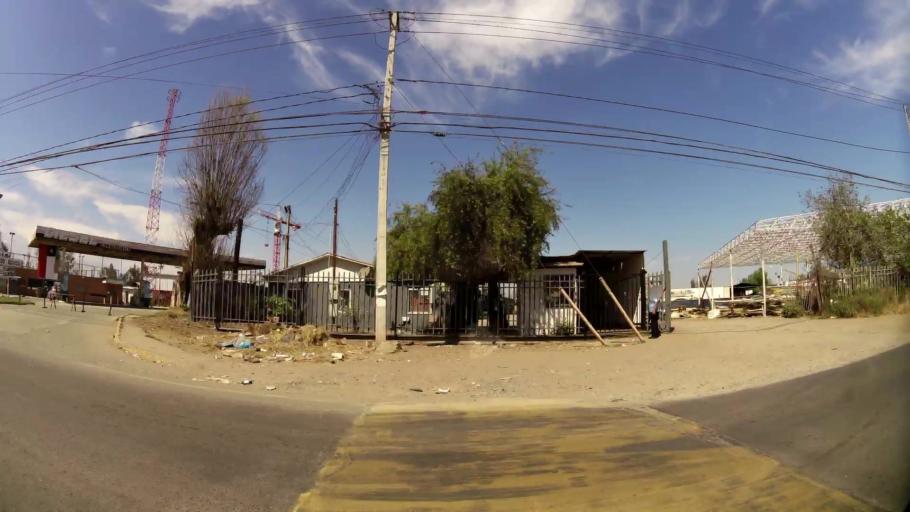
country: CL
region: Santiago Metropolitan
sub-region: Provincia de Santiago
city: Lo Prado
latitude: -33.4008
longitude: -70.7435
